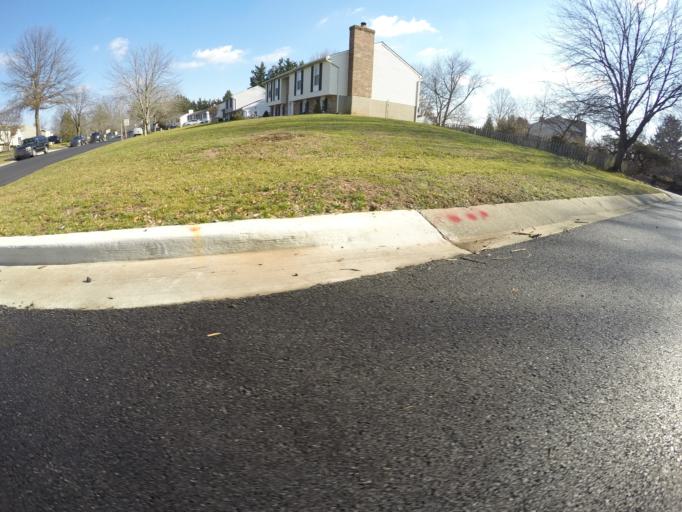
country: US
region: Maryland
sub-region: Howard County
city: Ilchester
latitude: 39.2165
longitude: -76.7924
